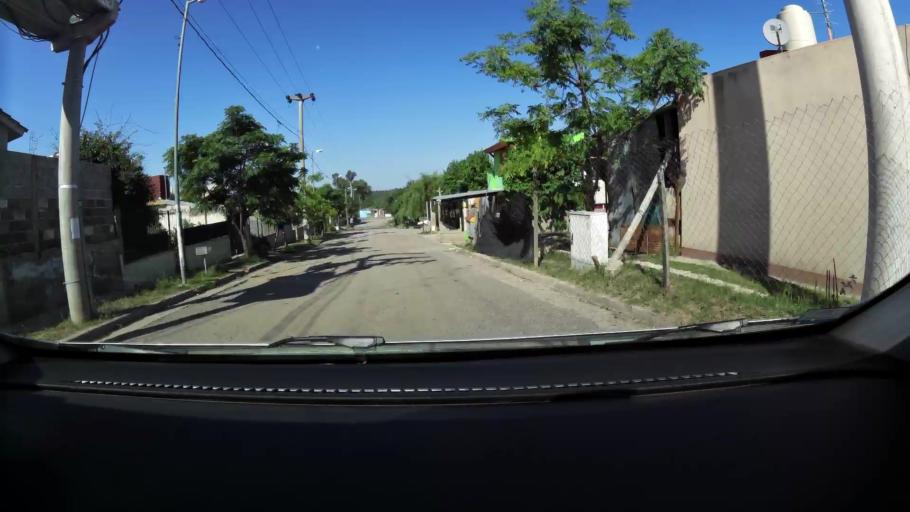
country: AR
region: Cordoba
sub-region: Departamento de Capital
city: Cordoba
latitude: -31.4023
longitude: -64.1503
